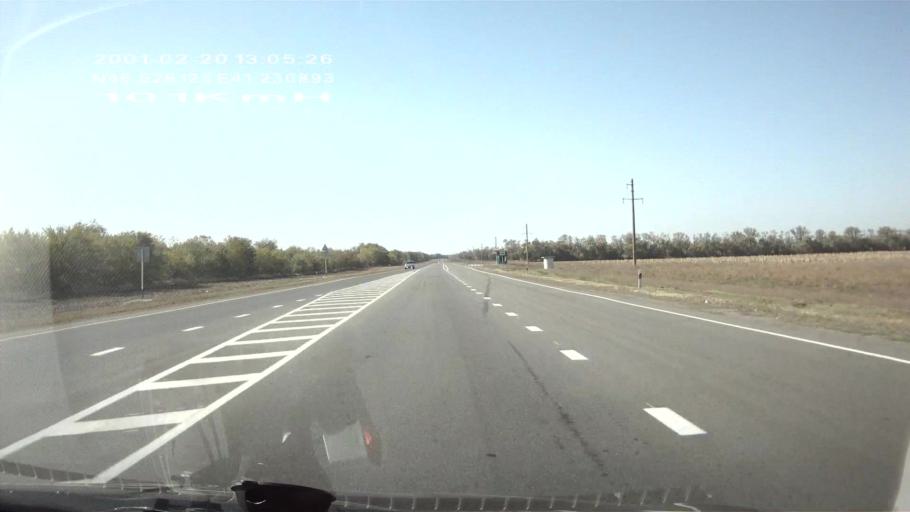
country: RU
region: Rostov
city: Gigant
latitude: 46.5265
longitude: 41.2292
